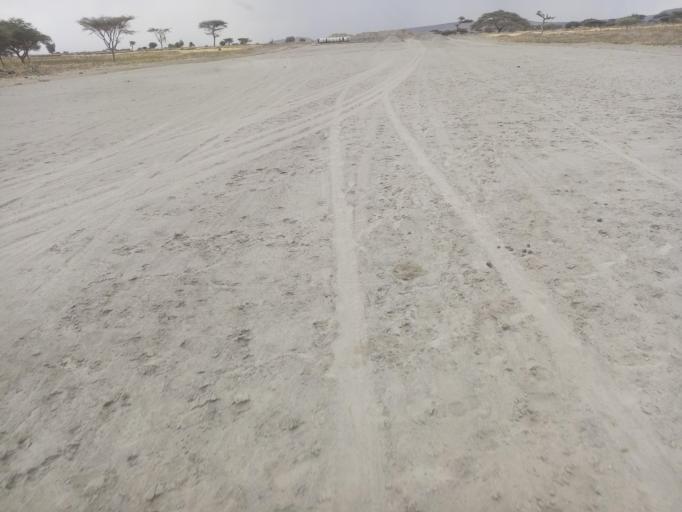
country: ET
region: Oromiya
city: Ziway
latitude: 7.8502
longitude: 38.6630
